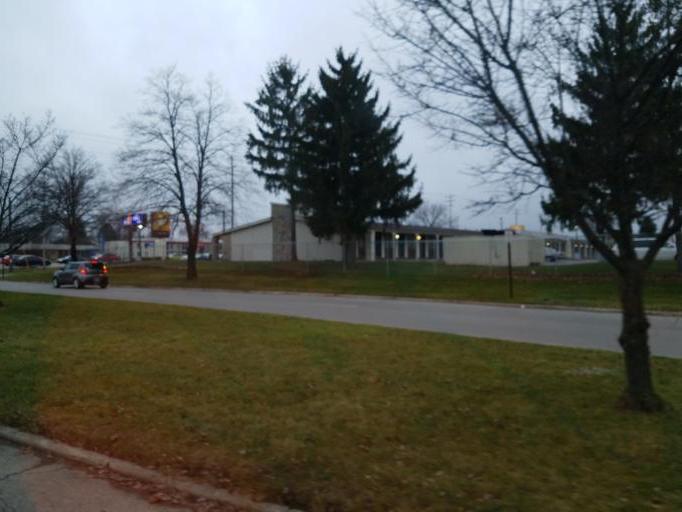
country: US
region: Ohio
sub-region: Franklin County
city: Worthington
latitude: 40.0882
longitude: -82.9810
